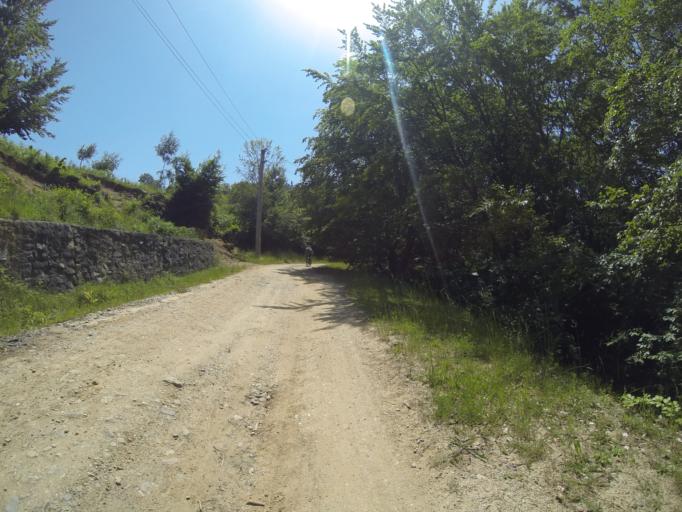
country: RO
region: Valcea
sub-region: Oras Baile Olanesti
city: Baile Olanesti
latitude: 45.2082
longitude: 24.2159
